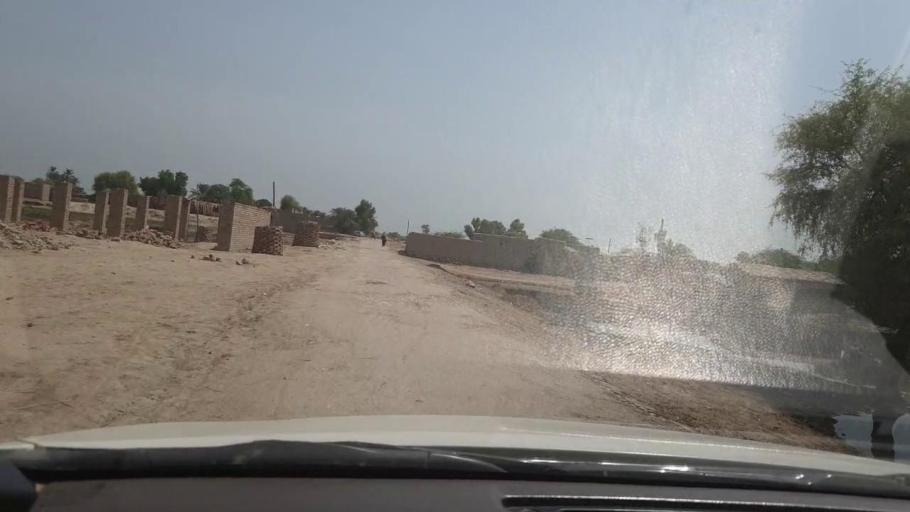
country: PK
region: Sindh
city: Shikarpur
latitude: 27.9441
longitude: 68.5975
